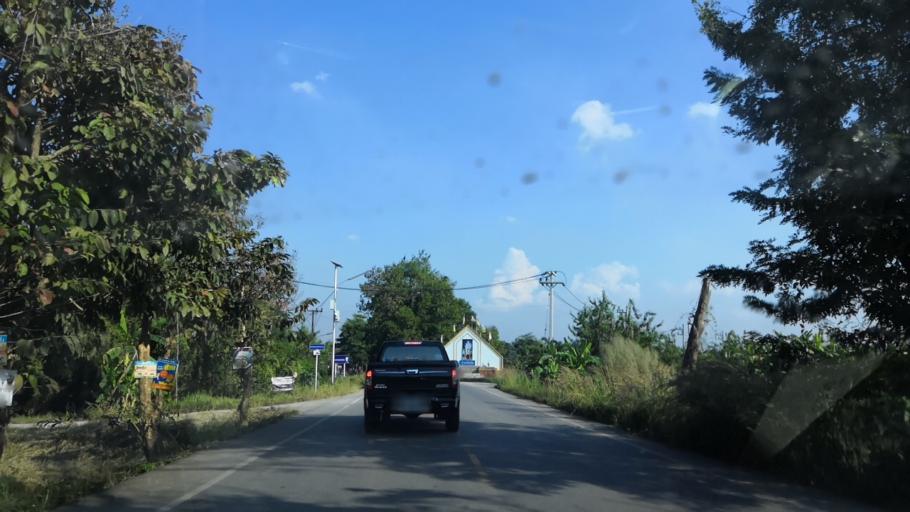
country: TH
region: Chiang Rai
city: Wiang Chai
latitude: 19.9326
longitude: 99.8931
